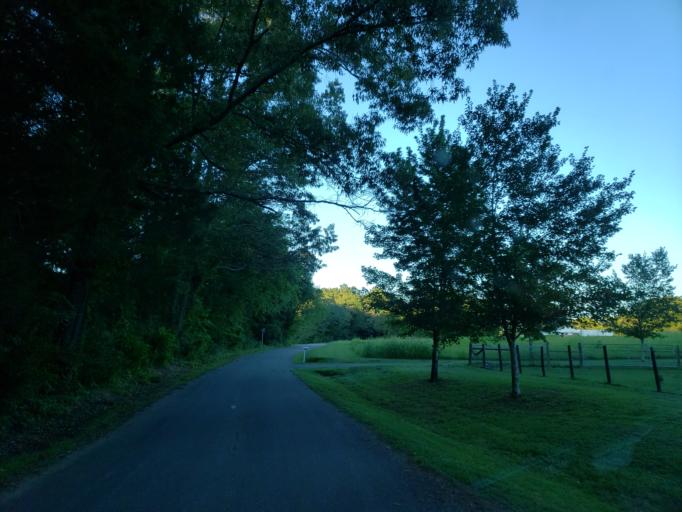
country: US
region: Georgia
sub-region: Bartow County
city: Euharlee
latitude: 34.0809
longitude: -84.9152
